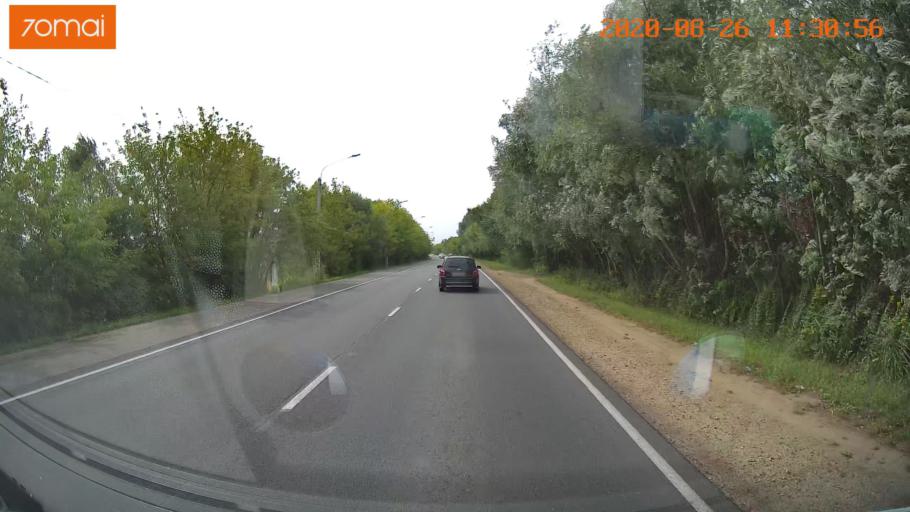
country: RU
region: Rjazan
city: Shilovo
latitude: 54.3113
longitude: 40.8778
